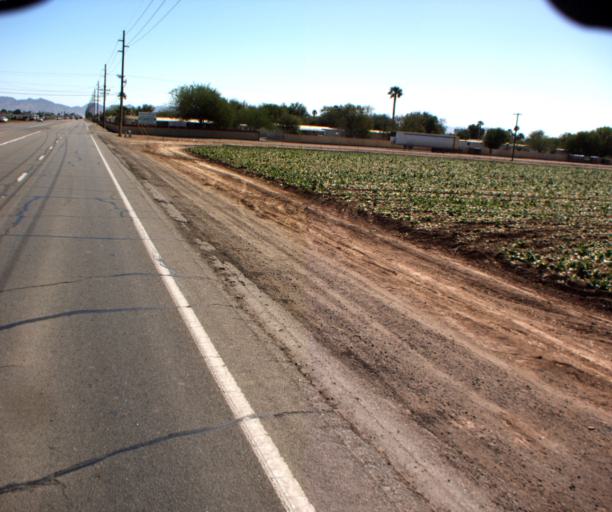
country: US
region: Arizona
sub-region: Yuma County
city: Yuma
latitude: 32.6989
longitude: -114.5485
